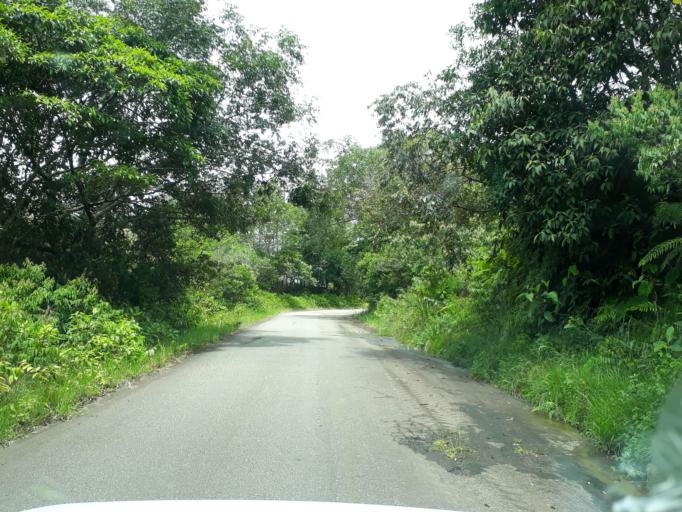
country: CO
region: Cundinamarca
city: Medina
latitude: 4.5792
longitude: -73.3432
